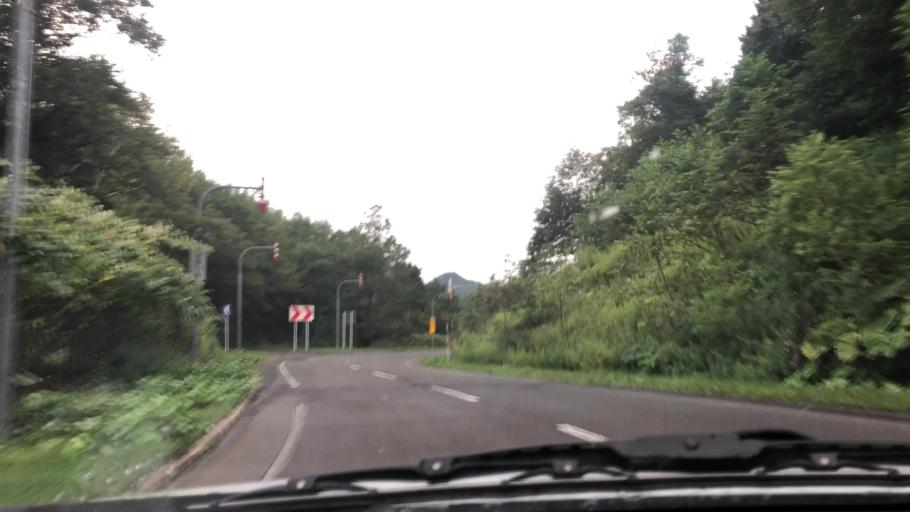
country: JP
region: Hokkaido
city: Shimo-furano
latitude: 42.9335
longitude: 142.3737
